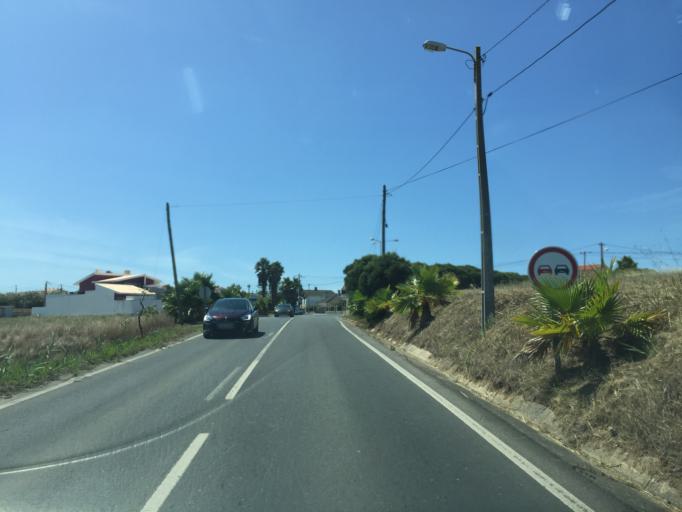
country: PT
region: Lisbon
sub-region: Lourinha
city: Lourinha
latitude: 39.2163
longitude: -9.3214
